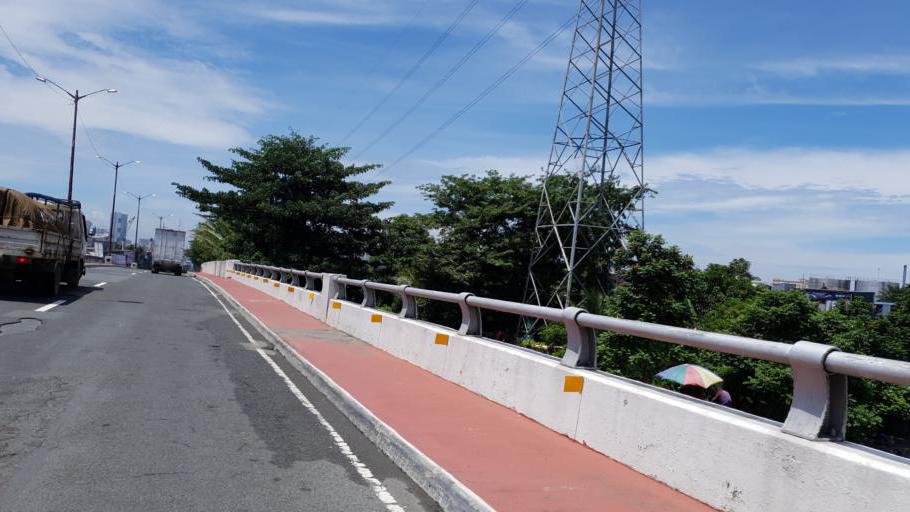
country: PH
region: Metro Manila
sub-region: San Juan
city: San Juan
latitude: 14.5940
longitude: 121.0122
